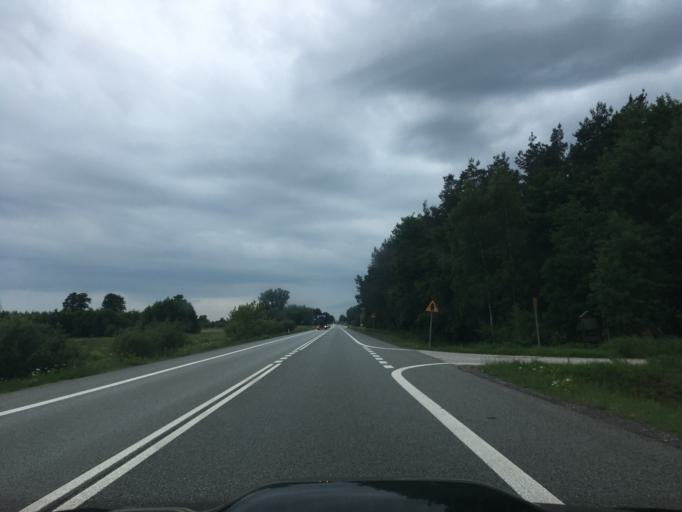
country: PL
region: Masovian Voivodeship
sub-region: Powiat otwocki
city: Karczew
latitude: 52.0285
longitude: 21.3142
